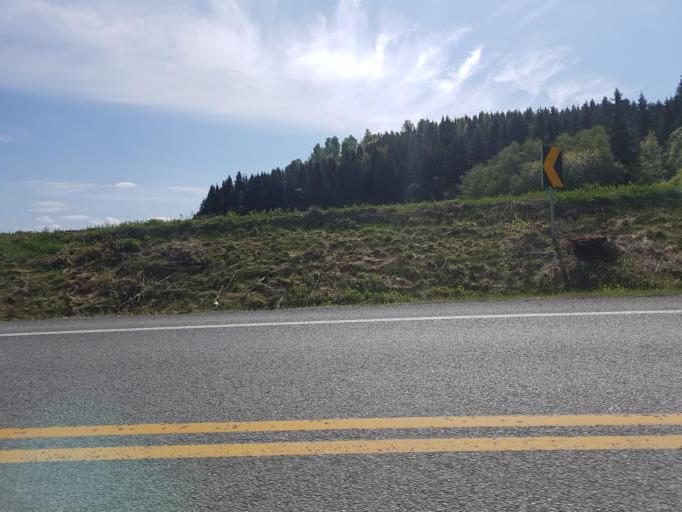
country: NO
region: Nord-Trondelag
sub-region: Levanger
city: Levanger
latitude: 63.7307
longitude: 11.2924
